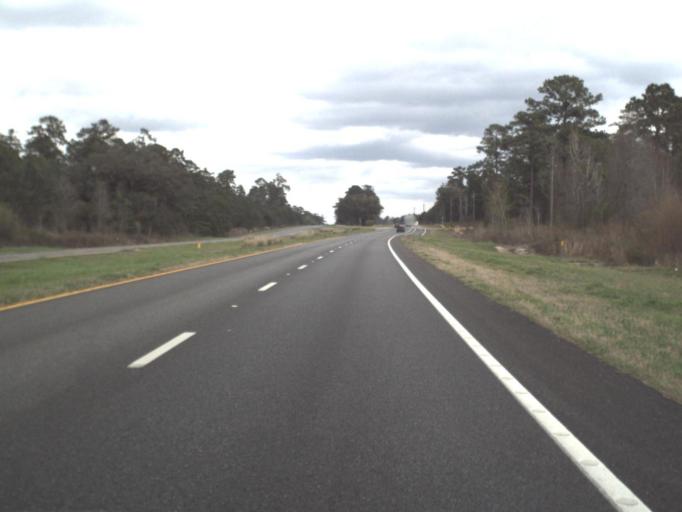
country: US
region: Florida
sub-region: Leon County
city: Tallahassee
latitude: 30.5909
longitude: -84.1918
